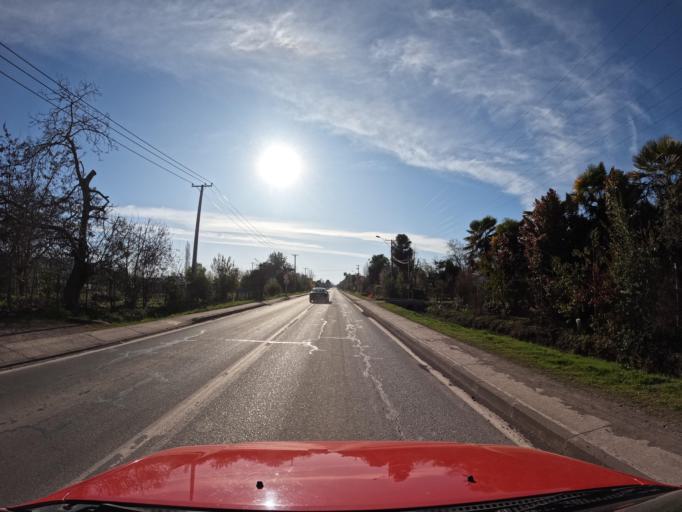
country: CL
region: Maule
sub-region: Provincia de Curico
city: Teno
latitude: -34.9609
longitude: -70.9695
